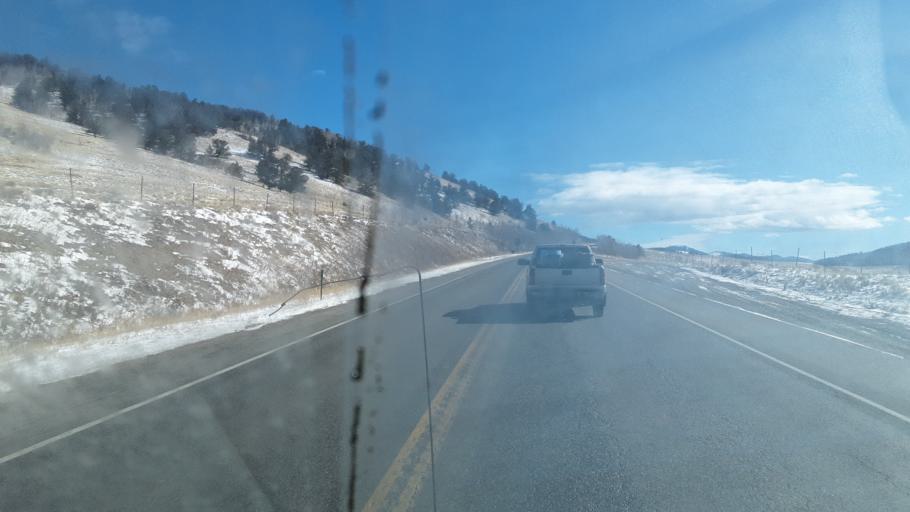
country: US
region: Colorado
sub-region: Summit County
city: Breckenridge
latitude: 39.4043
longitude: -105.7684
